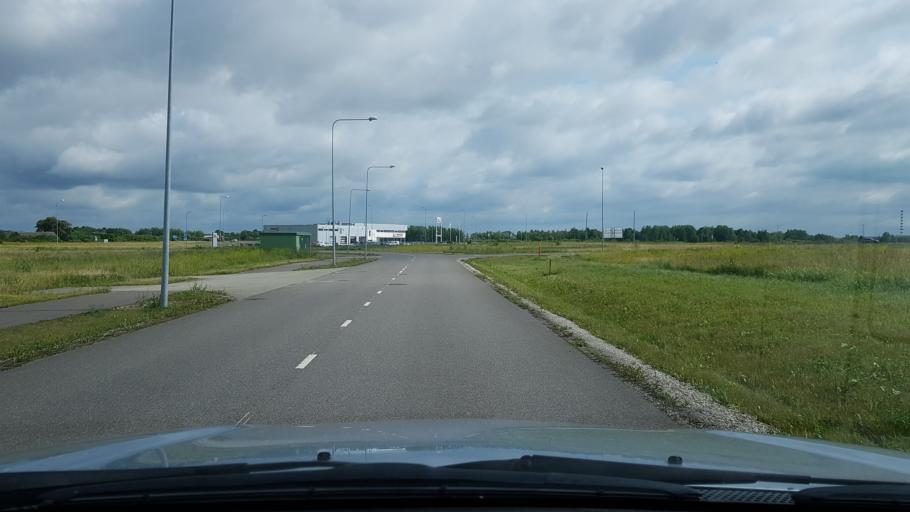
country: EE
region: Ida-Virumaa
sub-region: Narva linn
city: Narva
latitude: 59.3916
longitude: 28.1220
